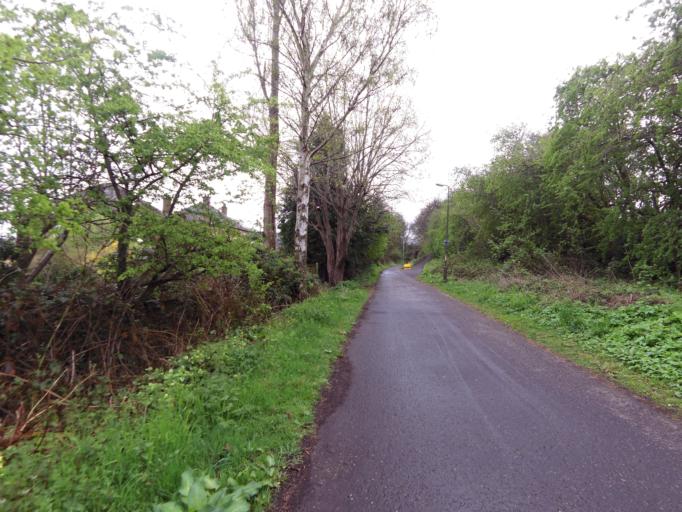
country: GB
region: Scotland
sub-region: Edinburgh
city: Edinburgh
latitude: 55.9528
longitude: -3.2393
